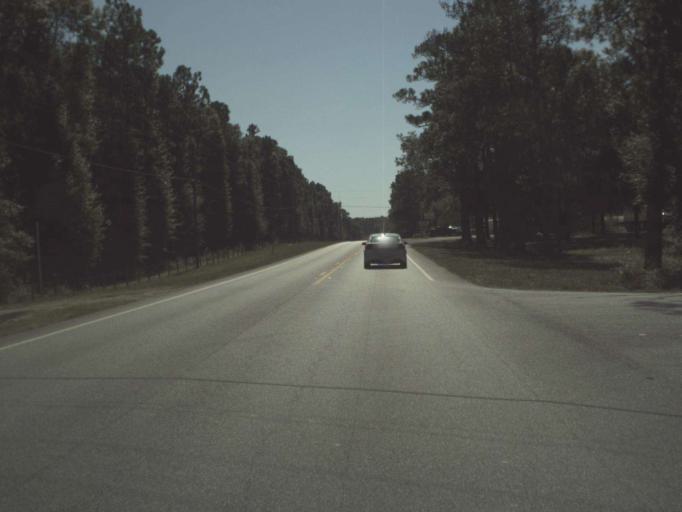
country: US
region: Florida
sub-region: Walton County
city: DeFuniak Springs
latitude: 30.7791
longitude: -86.1163
